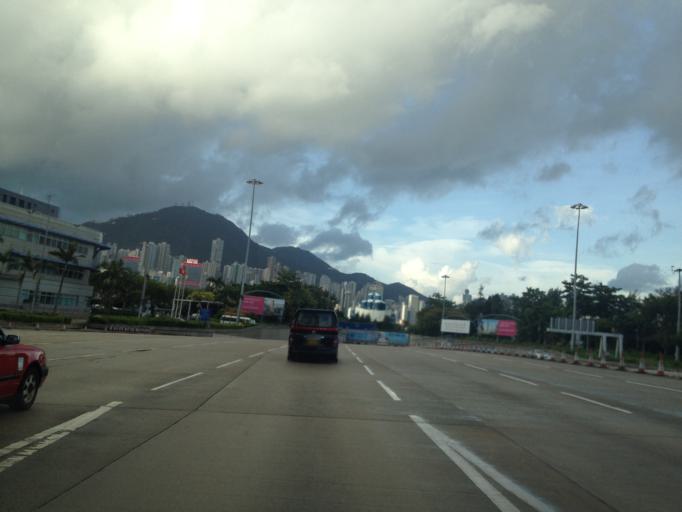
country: HK
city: Hong Kong
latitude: 22.3033
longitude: 114.1587
